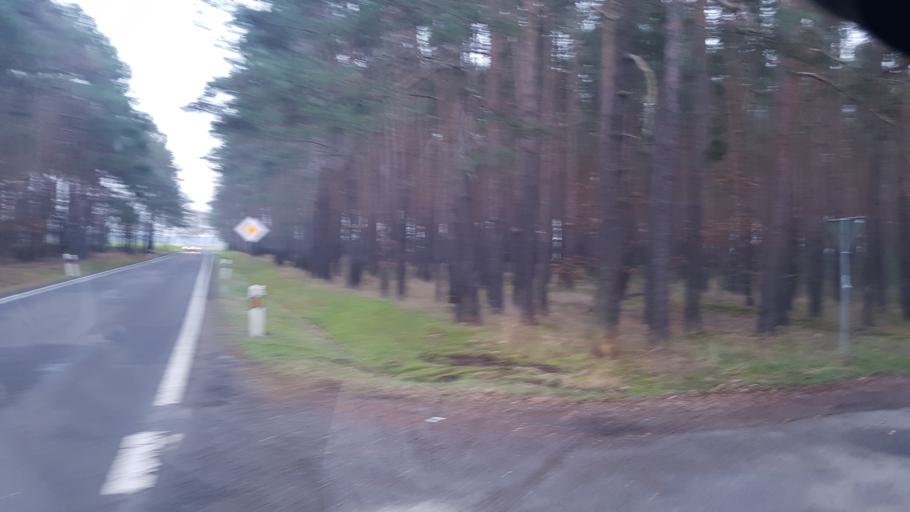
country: DE
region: Brandenburg
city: Drehnow
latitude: 51.8847
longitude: 14.3585
